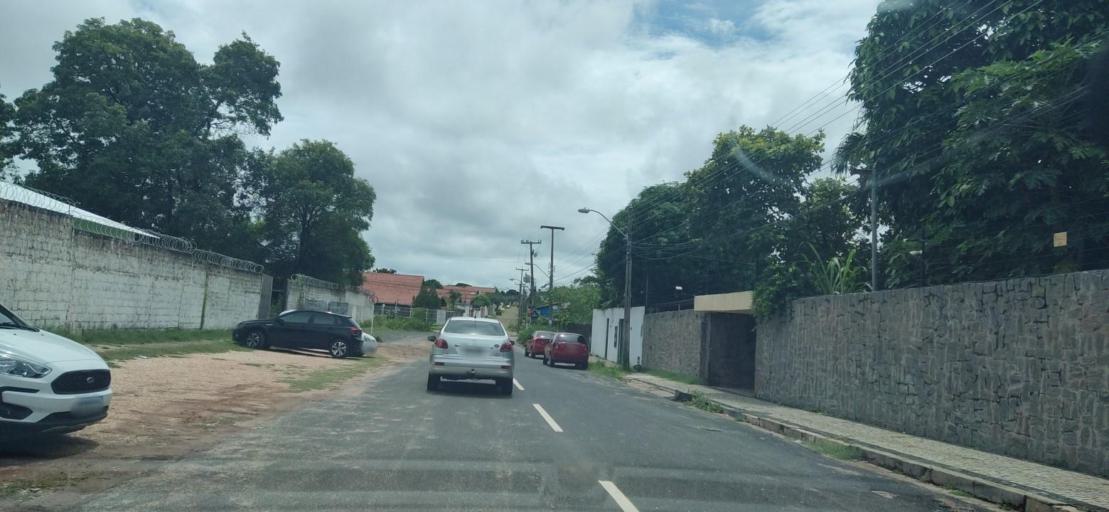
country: BR
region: Piaui
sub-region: Teresina
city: Teresina
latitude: -5.0723
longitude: -42.7700
